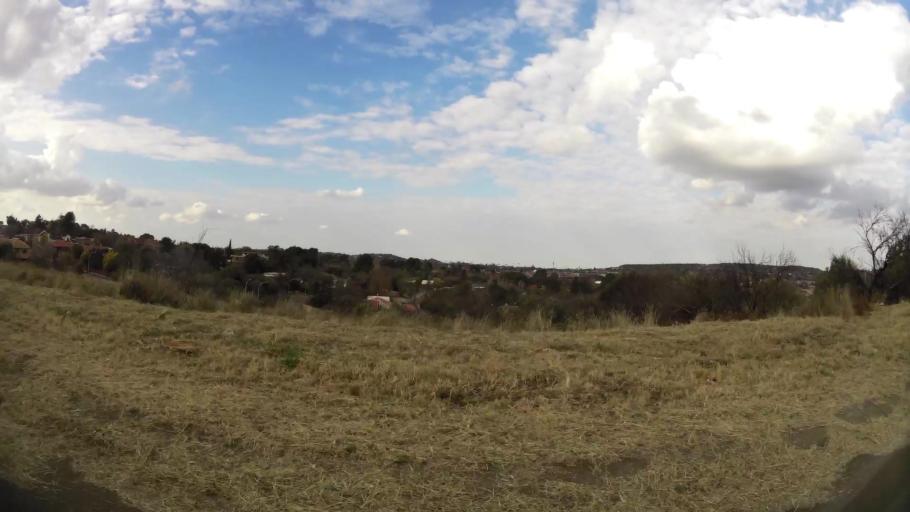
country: ZA
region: Orange Free State
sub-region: Mangaung Metropolitan Municipality
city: Bloemfontein
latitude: -29.0876
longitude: 26.2019
